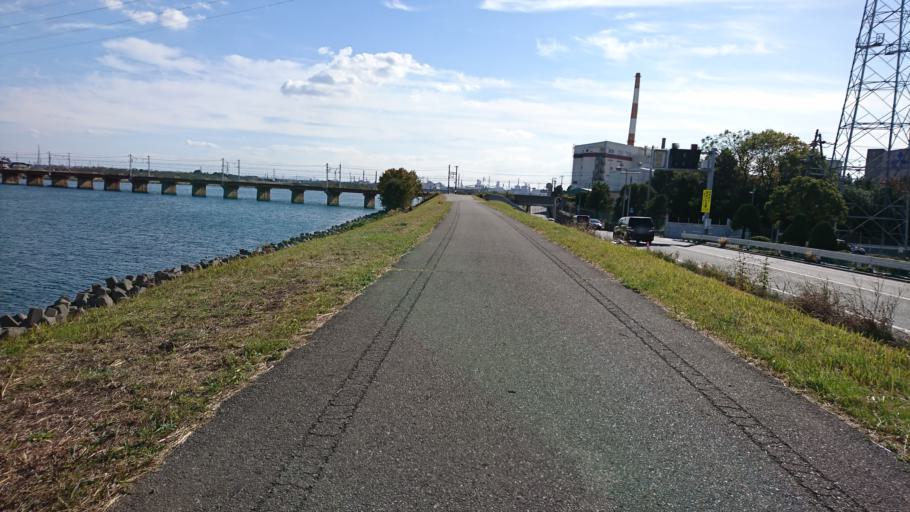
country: JP
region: Hyogo
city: Kakogawacho-honmachi
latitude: 34.7540
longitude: 134.8060
